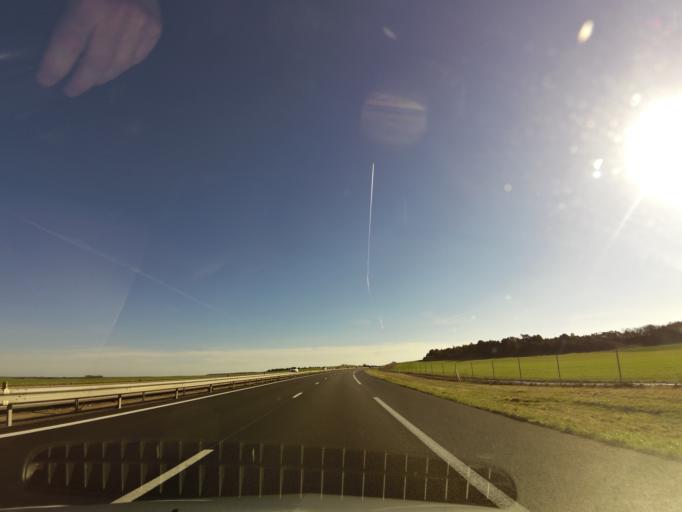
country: FR
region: Bourgogne
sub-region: Departement de l'Yonne
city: Joux-la-Ville
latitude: 47.6520
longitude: 3.9028
